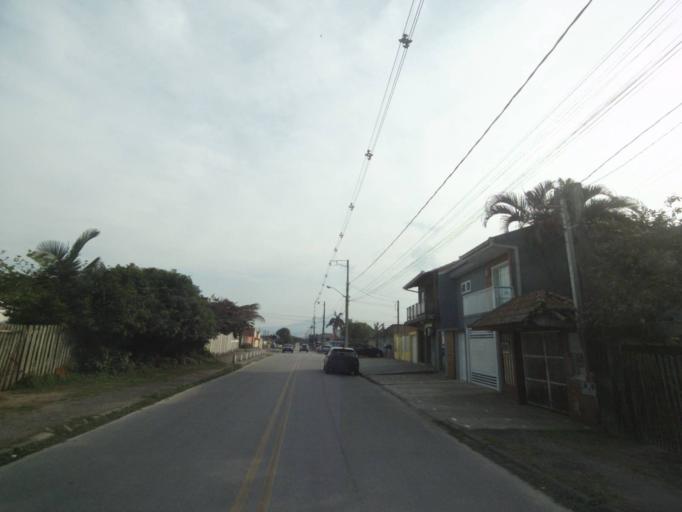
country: BR
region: Parana
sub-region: Paranagua
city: Paranagua
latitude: -25.5232
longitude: -48.5337
